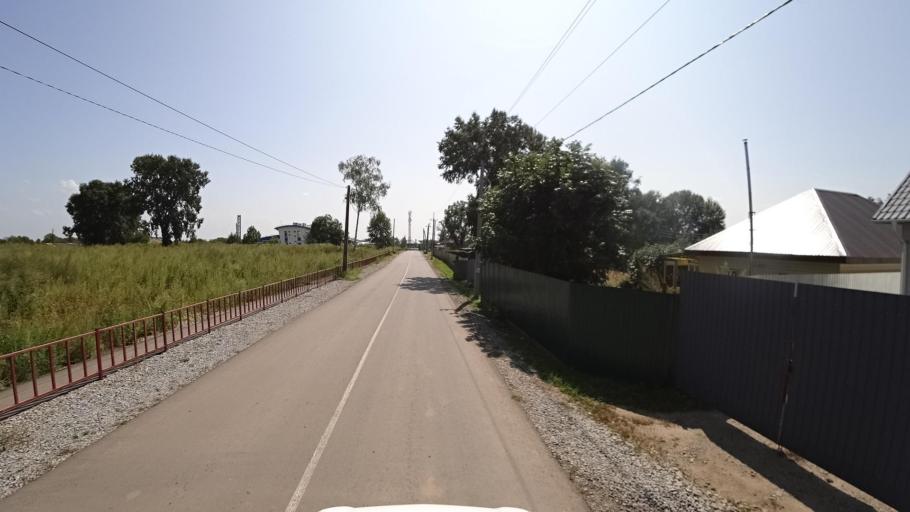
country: RU
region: Khabarovsk Krai
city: Khor
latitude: 47.9637
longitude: 135.1162
